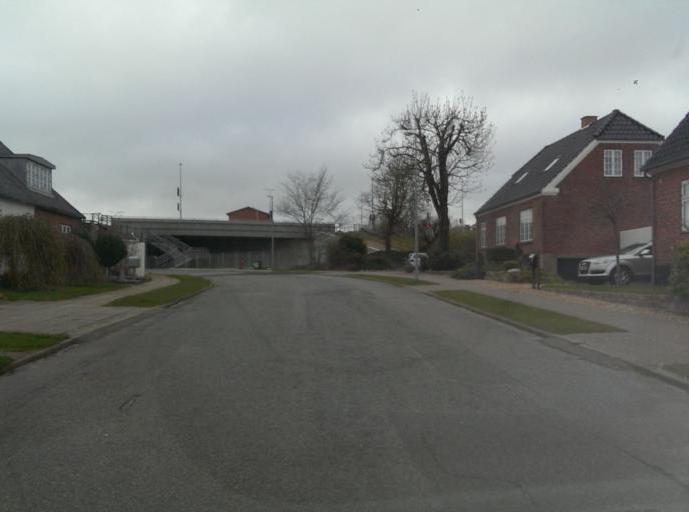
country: DK
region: South Denmark
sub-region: Esbjerg Kommune
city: Esbjerg
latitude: 55.4744
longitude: 8.4813
